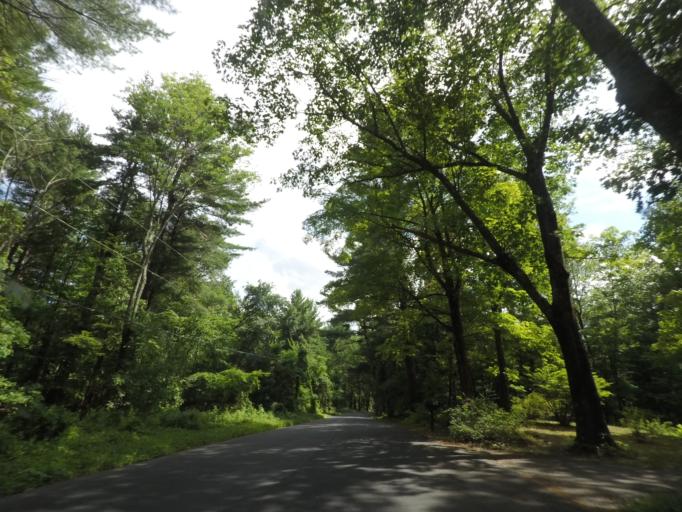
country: US
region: New York
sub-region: Rensselaer County
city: Averill Park
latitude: 42.6543
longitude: -73.5503
